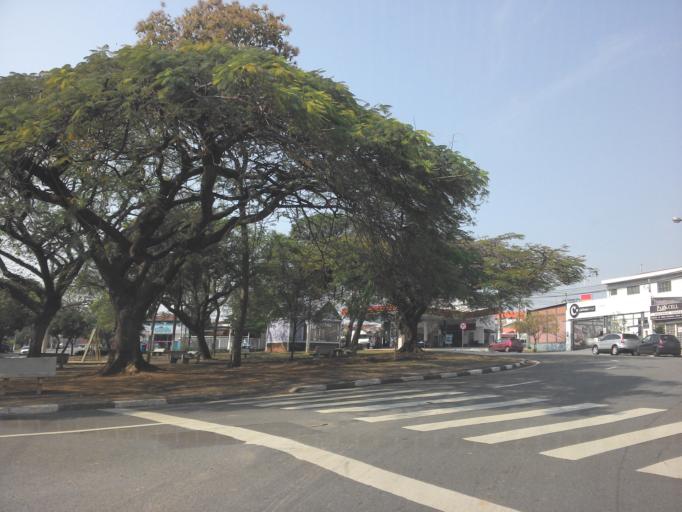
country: BR
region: Sao Paulo
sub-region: Campinas
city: Campinas
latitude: -22.9222
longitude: -47.0836
